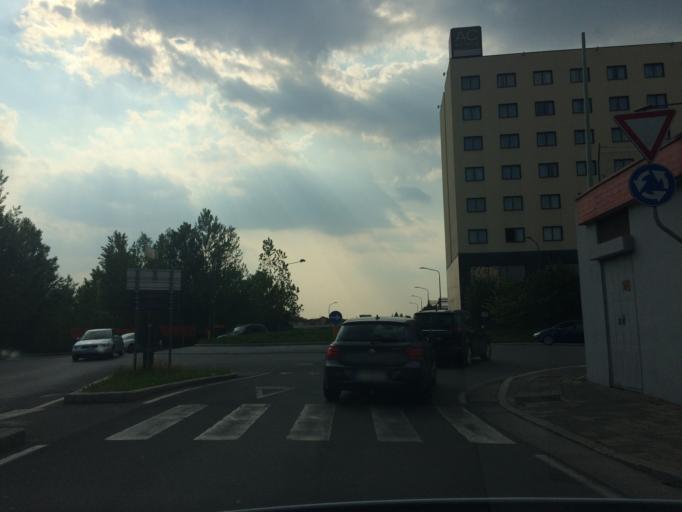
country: IT
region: Lombardy
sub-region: Provincia di Brescia
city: Brescia
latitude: 45.5368
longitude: 10.2038
